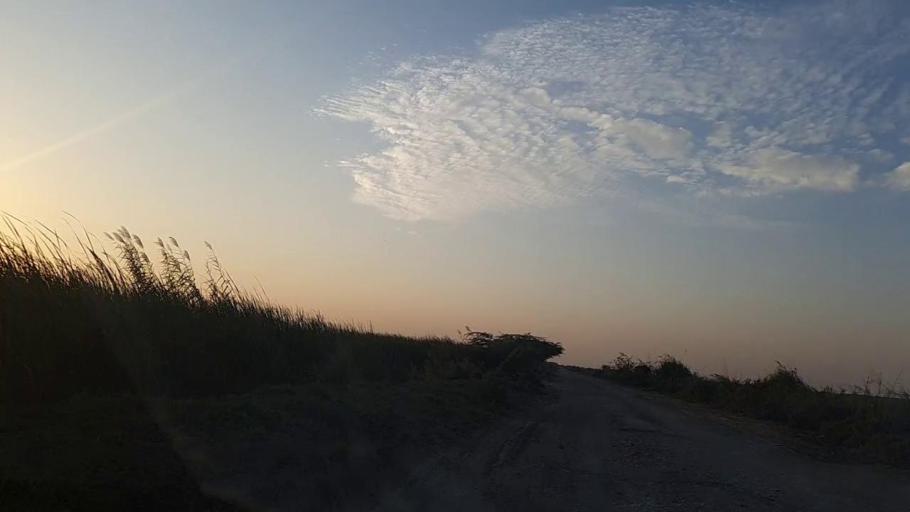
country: PK
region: Sindh
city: Chuhar Jamali
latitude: 24.4649
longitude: 68.1007
